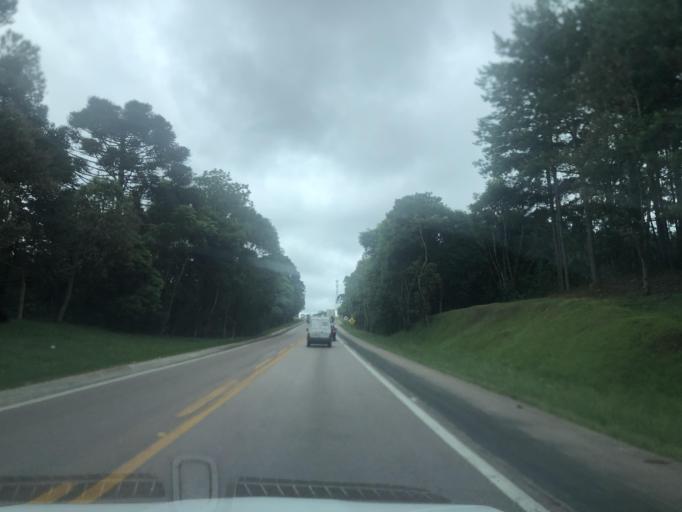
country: BR
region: Parana
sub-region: Araucaria
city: Araucaria
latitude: -25.8659
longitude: -49.4393
